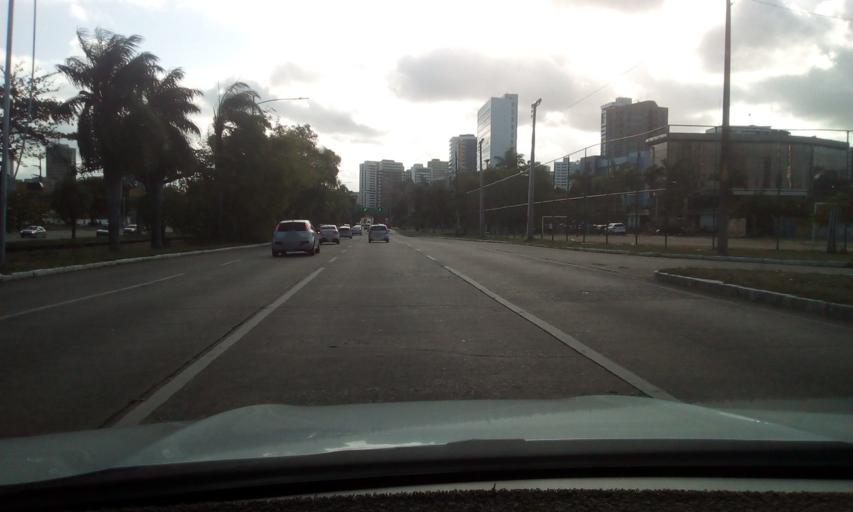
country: BR
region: Pernambuco
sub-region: Recife
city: Recife
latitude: -8.0424
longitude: -34.8851
